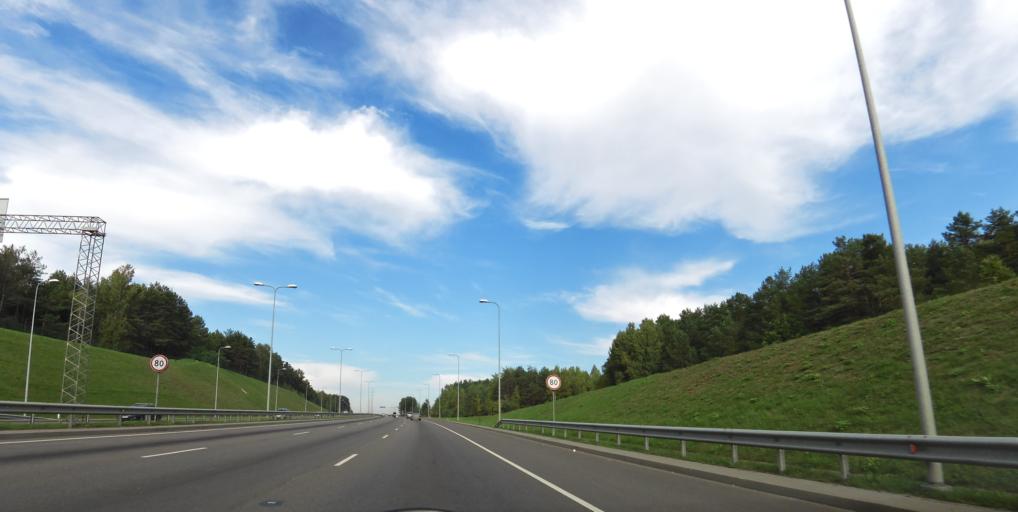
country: LT
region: Vilnius County
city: Lazdynai
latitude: 54.6756
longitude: 25.1962
